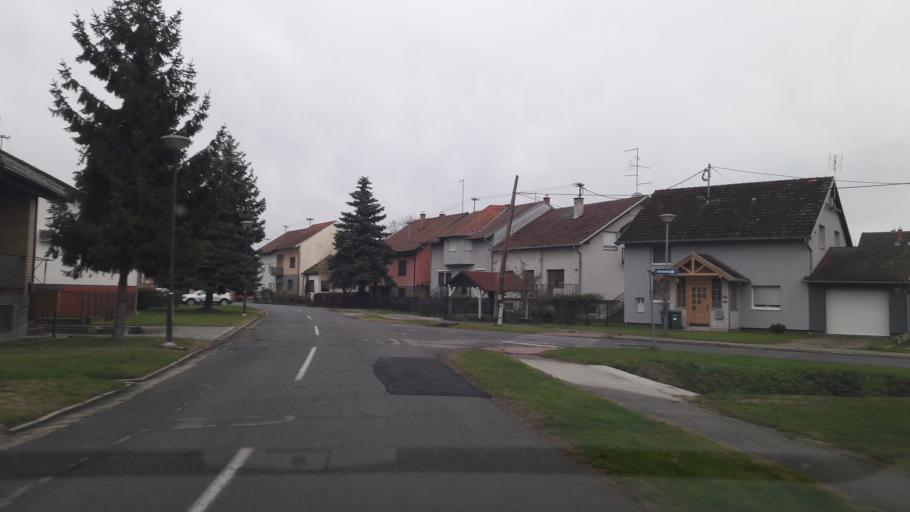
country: HR
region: Osjecko-Baranjska
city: Visnjevac
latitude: 45.5669
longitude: 18.6241
